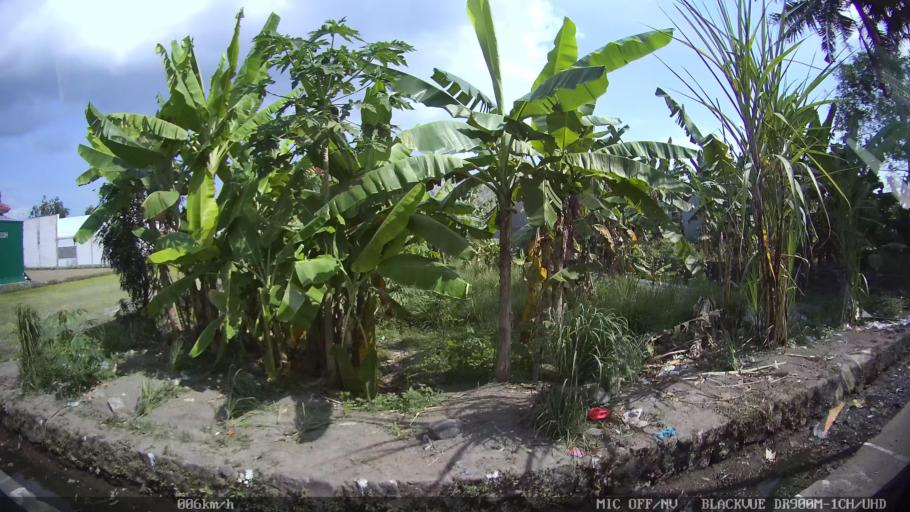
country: ID
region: Daerah Istimewa Yogyakarta
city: Kasihan
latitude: -7.8148
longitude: 110.3310
